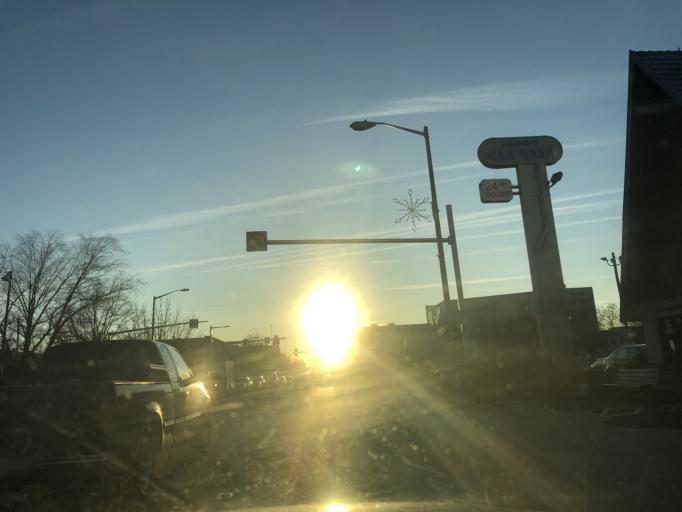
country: US
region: Pennsylvania
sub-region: Montgomery County
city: Ardmore
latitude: 40.0094
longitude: -75.2940
